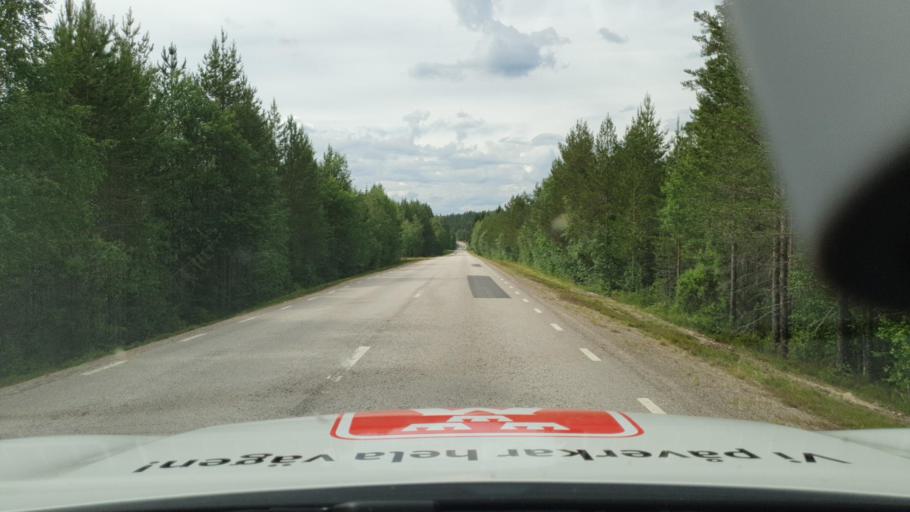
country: NO
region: Hedmark
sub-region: Trysil
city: Innbygda
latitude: 60.9249
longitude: 12.5220
